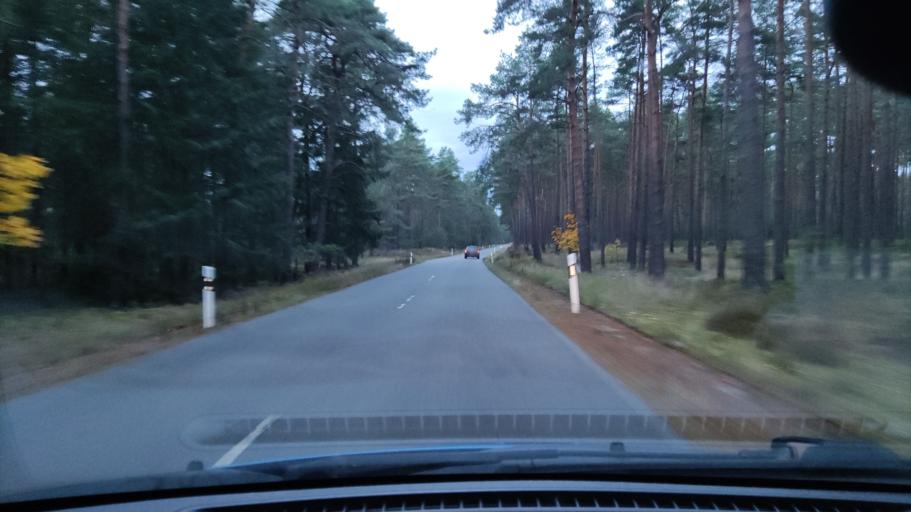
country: DE
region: Lower Saxony
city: Gorleben
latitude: 53.0167
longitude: 11.3880
